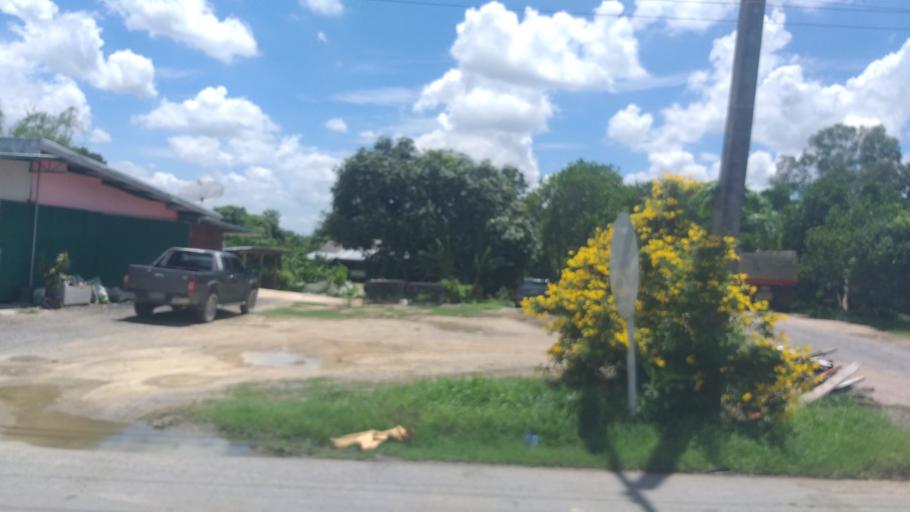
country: TH
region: Nakhon Nayok
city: Ban Na
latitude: 14.2890
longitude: 101.0674
